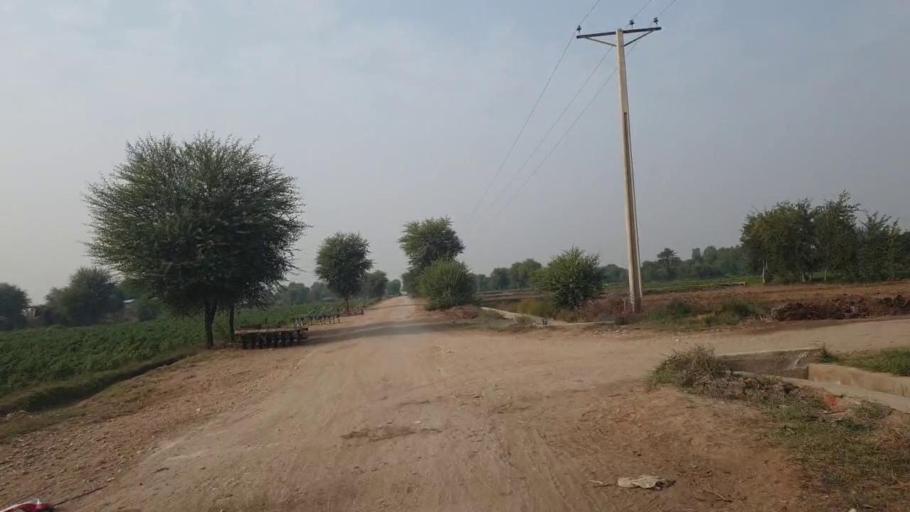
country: PK
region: Sindh
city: Sann
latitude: 26.0667
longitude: 68.1166
